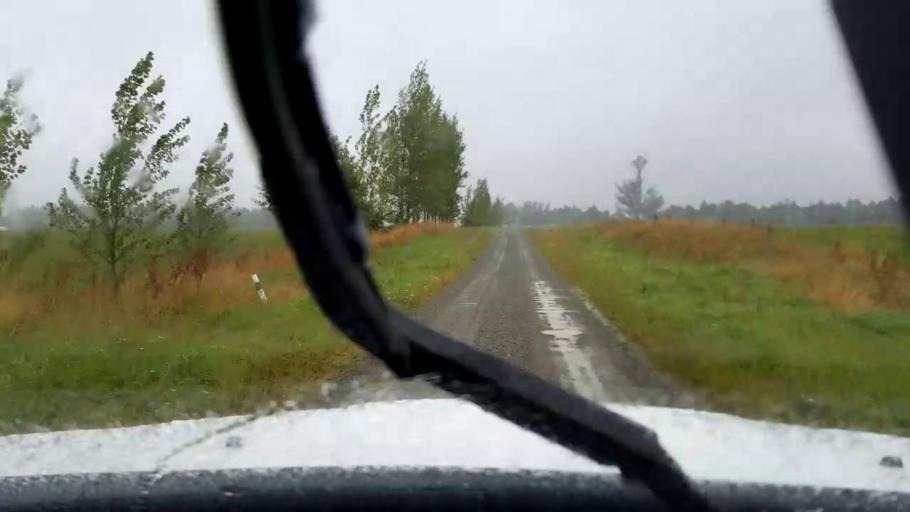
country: NZ
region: Canterbury
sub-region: Timaru District
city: Pleasant Point
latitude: -44.1989
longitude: 171.0906
